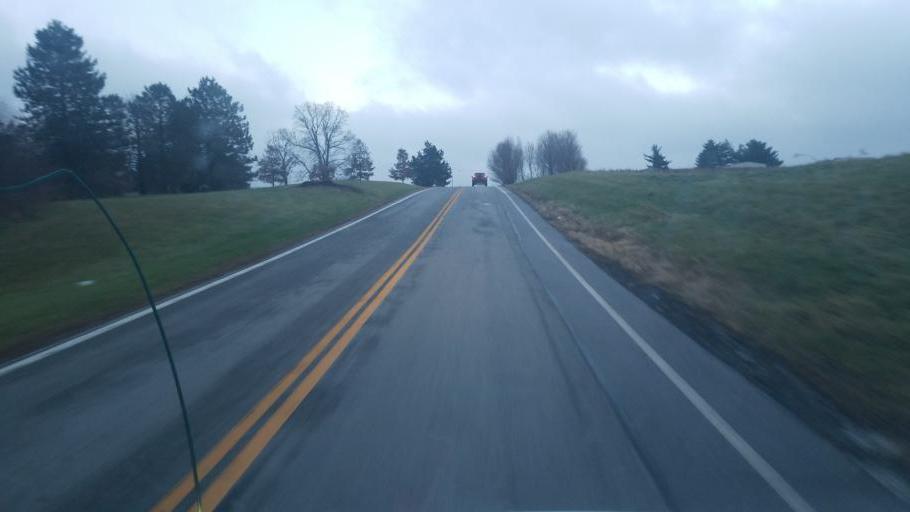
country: US
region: Ohio
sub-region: Wyandot County
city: Upper Sandusky
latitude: 40.9150
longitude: -83.1313
